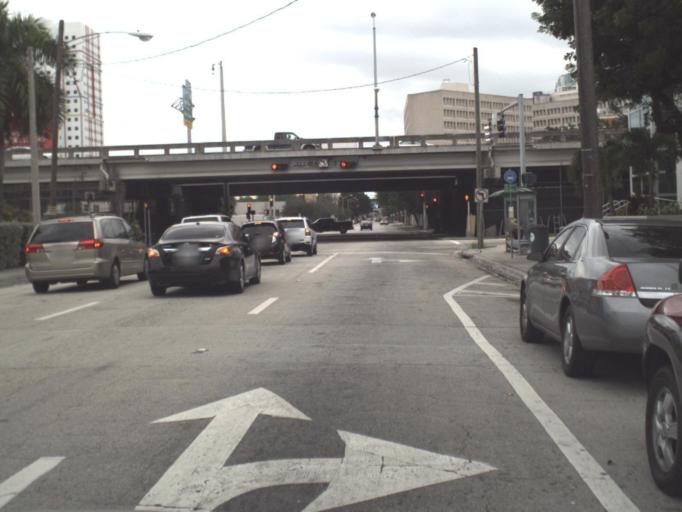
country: US
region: Florida
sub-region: Miami-Dade County
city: Miami
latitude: 25.7787
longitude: -80.2007
